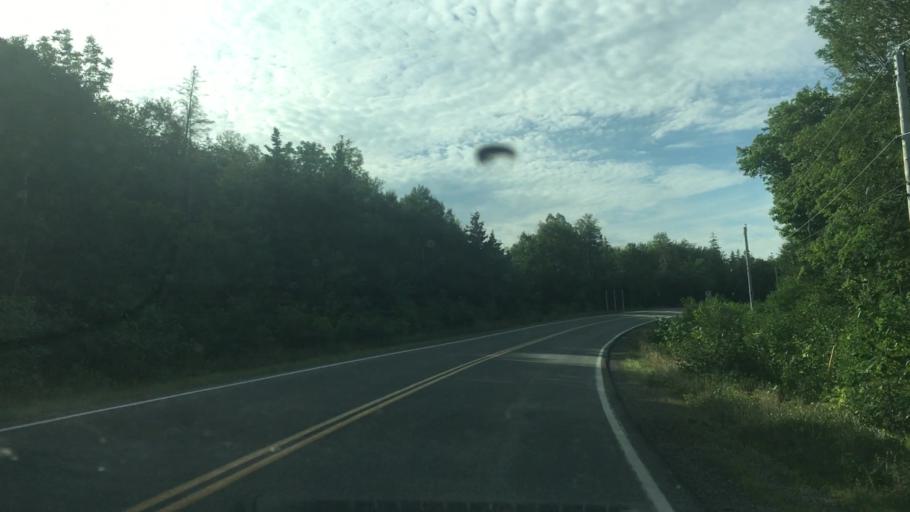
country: CA
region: Nova Scotia
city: Sydney Mines
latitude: 46.8177
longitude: -60.7940
